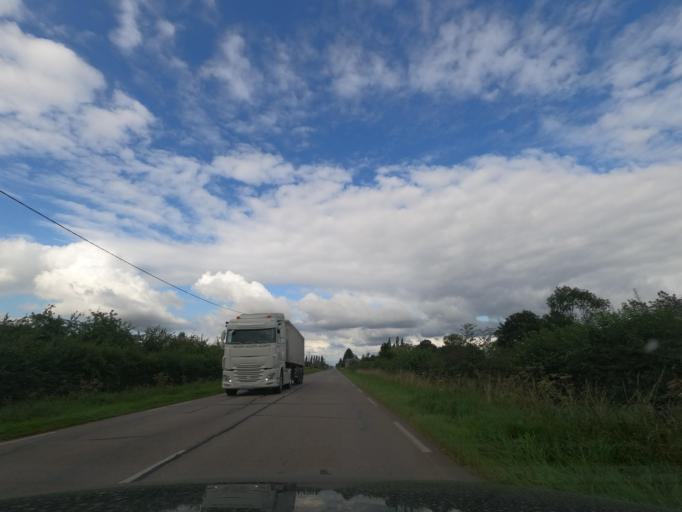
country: FR
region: Lower Normandy
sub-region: Departement du Calvados
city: Orbec
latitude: 48.9091
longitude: 0.4177
